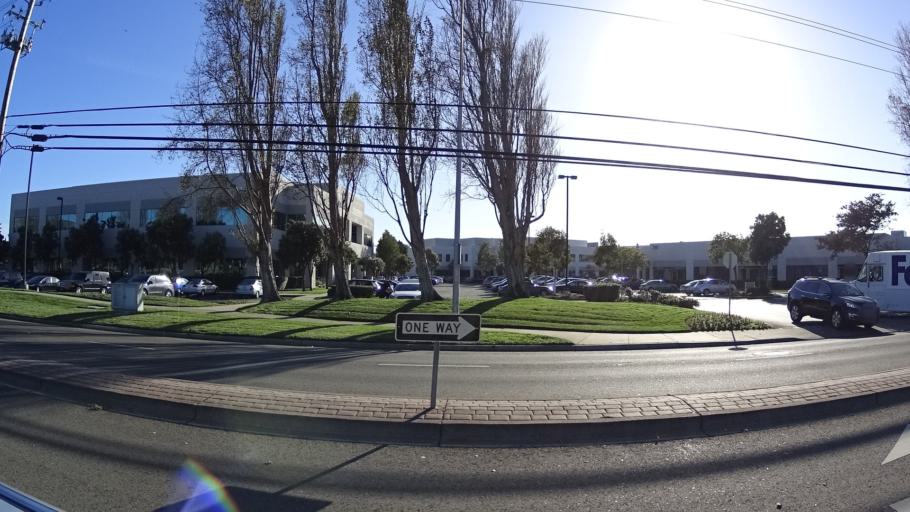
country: US
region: California
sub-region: San Mateo County
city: South San Francisco
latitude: 37.6532
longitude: -122.3949
